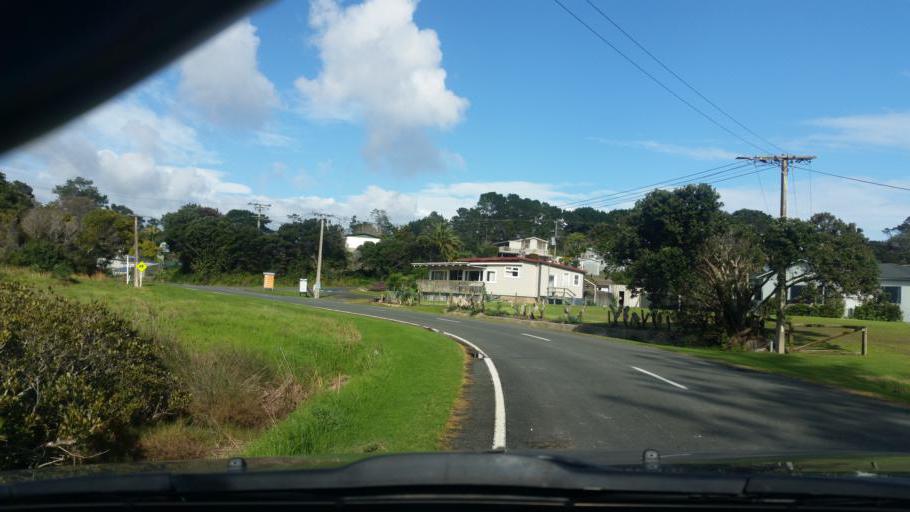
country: NZ
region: Auckland
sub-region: Auckland
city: Wellsford
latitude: -36.2537
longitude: 174.2456
